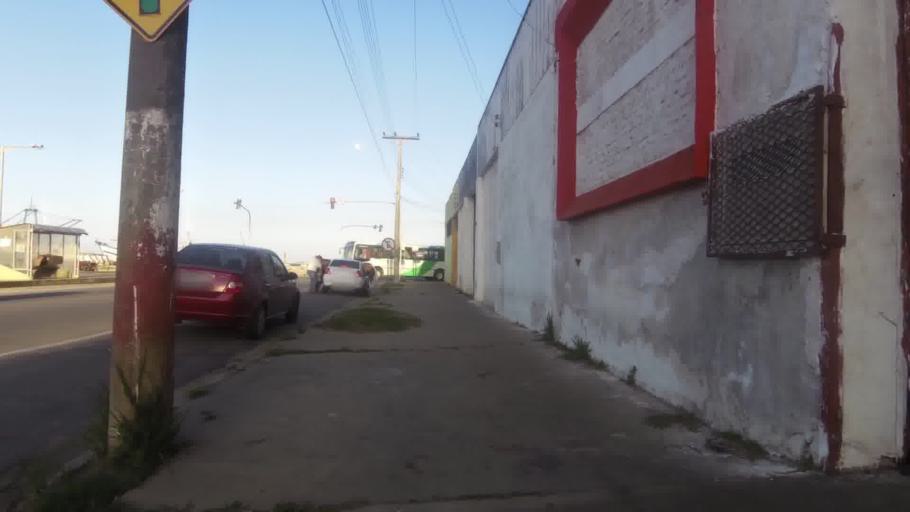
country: BR
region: Rio Grande do Sul
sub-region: Rio Grande
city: Rio Grande
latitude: -32.0285
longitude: -52.1013
